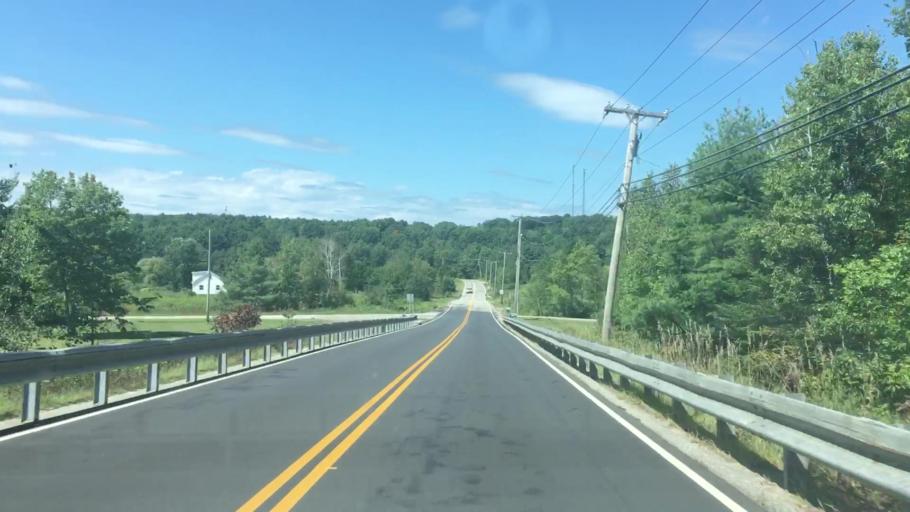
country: US
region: Maine
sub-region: Androscoggin County
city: Sabattus
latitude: 44.0792
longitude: -70.1230
